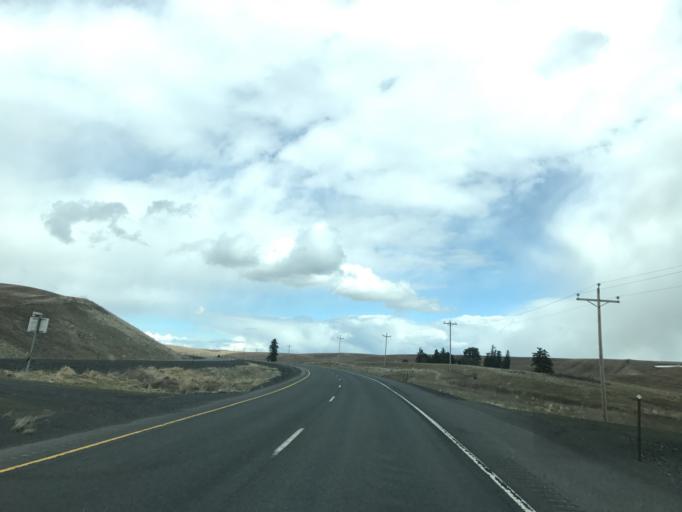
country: US
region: Idaho
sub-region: Nez Perce County
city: Lewiston
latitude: 46.4947
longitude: -117.0053
